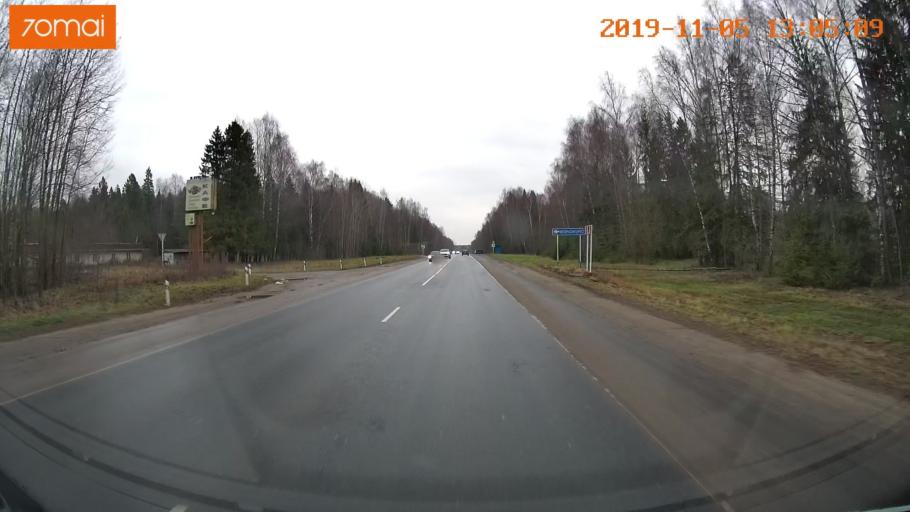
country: RU
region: Ivanovo
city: Kitovo
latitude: 56.8844
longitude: 41.2368
